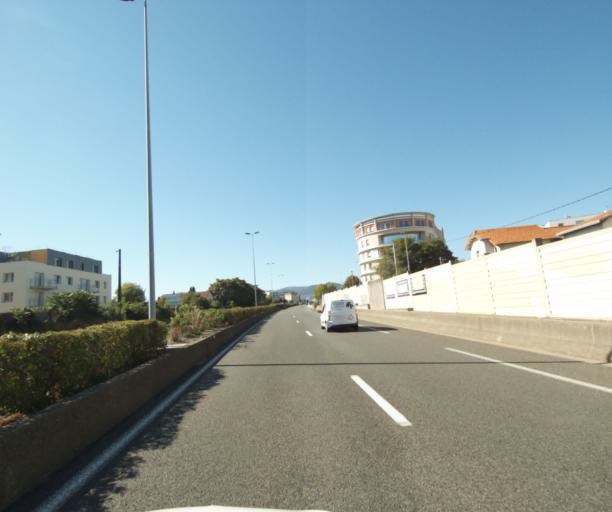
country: FR
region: Auvergne
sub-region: Departement du Puy-de-Dome
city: Aubiere
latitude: 45.7684
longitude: 3.1106
